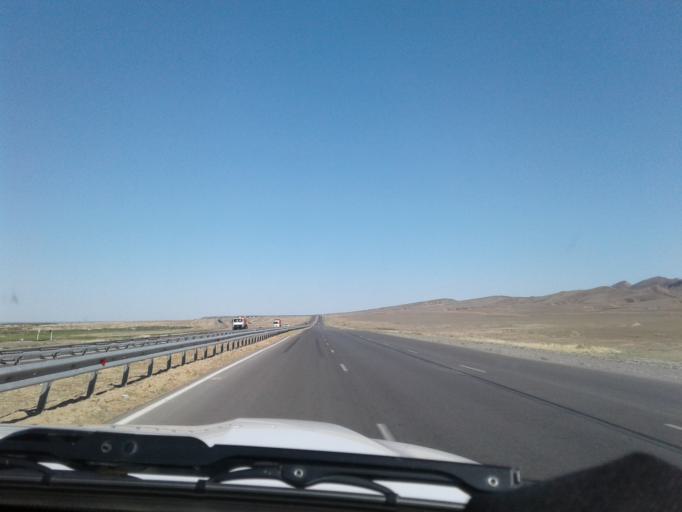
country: IR
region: Razavi Khorasan
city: Dargaz
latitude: 37.6951
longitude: 59.0525
